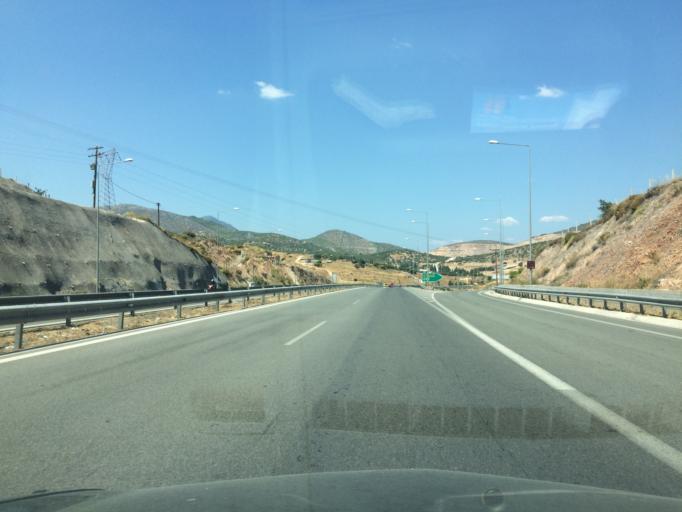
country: GR
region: Central Greece
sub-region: Nomos Evvoias
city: Vathi
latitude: 38.4129
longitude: 23.5922
